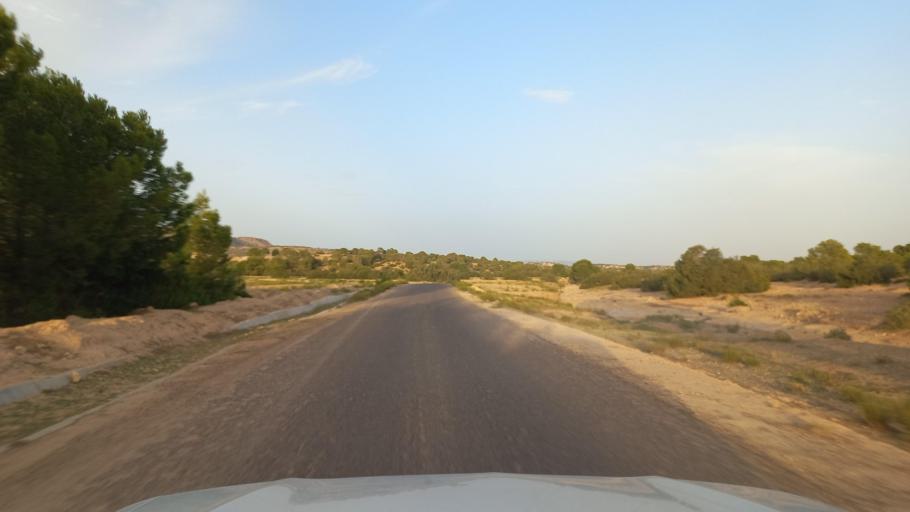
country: TN
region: Al Qasrayn
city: Sbiba
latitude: 35.4107
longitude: 8.9243
